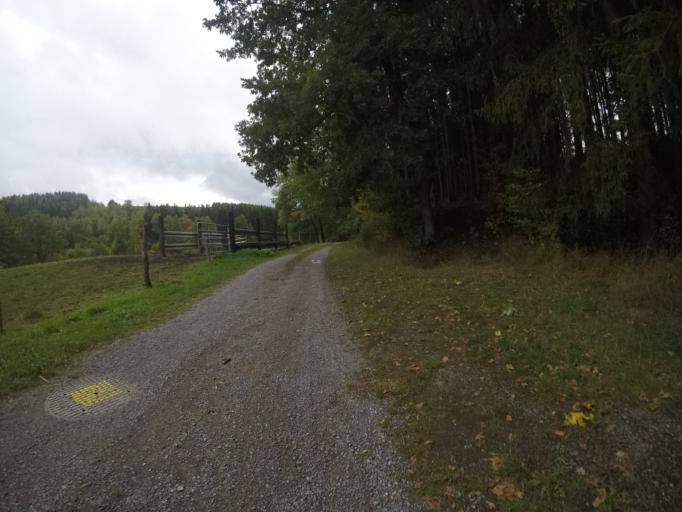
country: BE
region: Wallonia
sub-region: Province du Luxembourg
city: Fauvillers
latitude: 49.8965
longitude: 5.6870
